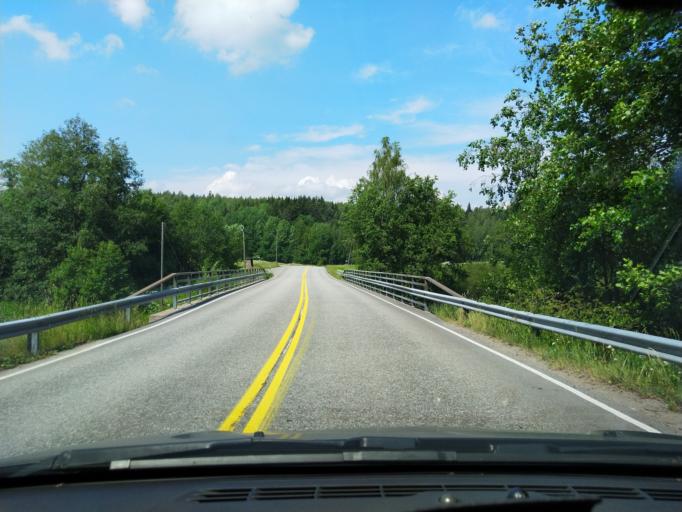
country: FI
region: Uusimaa
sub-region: Helsinki
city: Lohja
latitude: 60.3354
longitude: 24.0671
